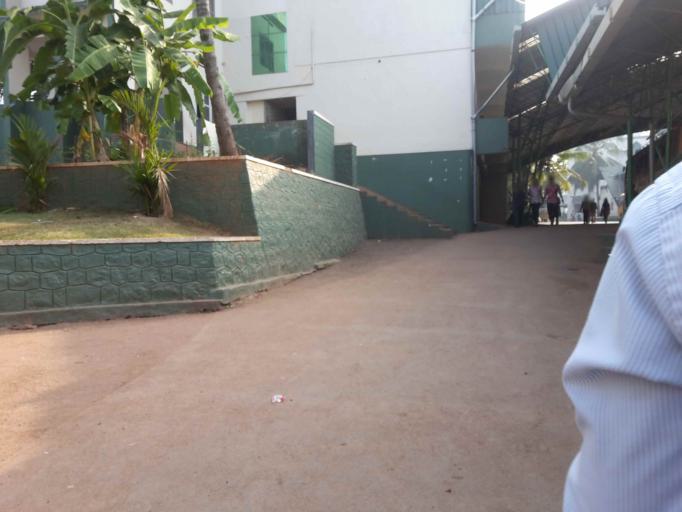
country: IN
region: Kerala
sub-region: Kozhikode
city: Kunnamangalam
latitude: 11.2935
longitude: 75.8235
